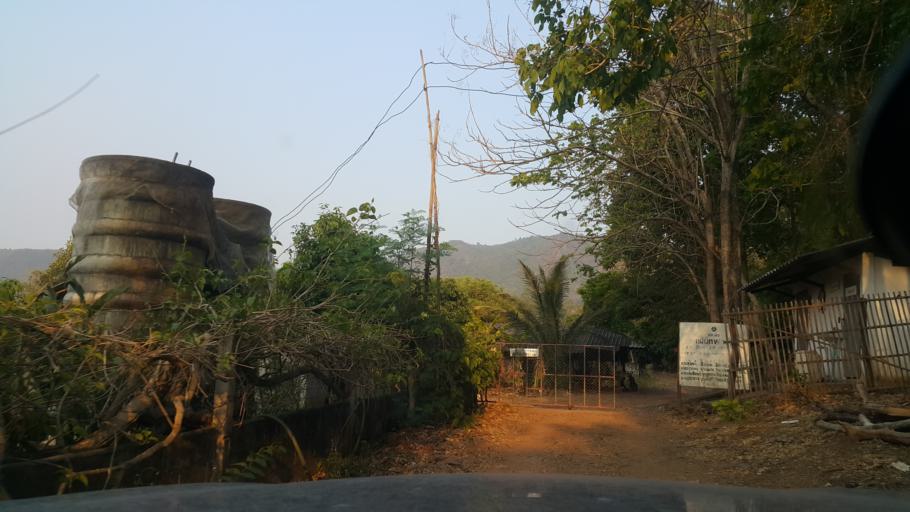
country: TH
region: Chiang Mai
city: Mae On
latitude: 18.7407
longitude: 99.2536
